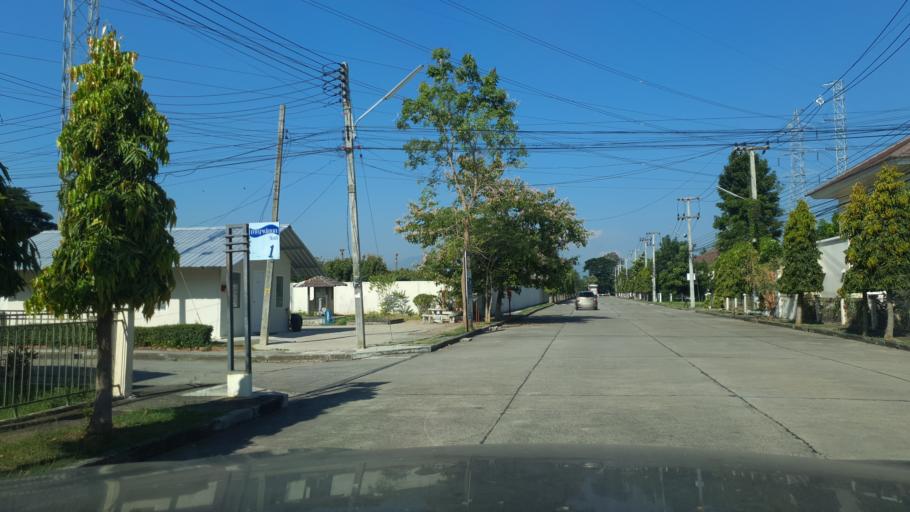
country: TH
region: Chiang Mai
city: Saraphi
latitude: 18.7335
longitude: 99.0754
